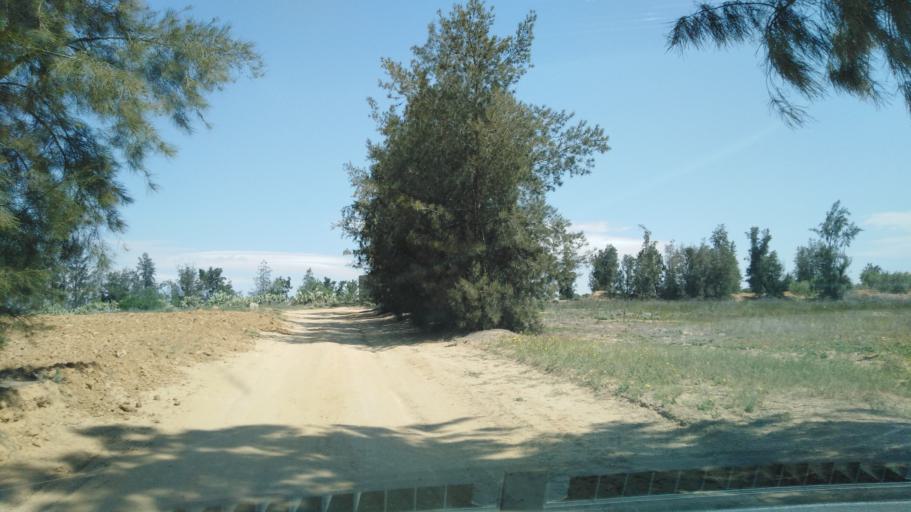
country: TN
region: Safaqis
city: Sfax
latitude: 34.7711
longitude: 10.5279
